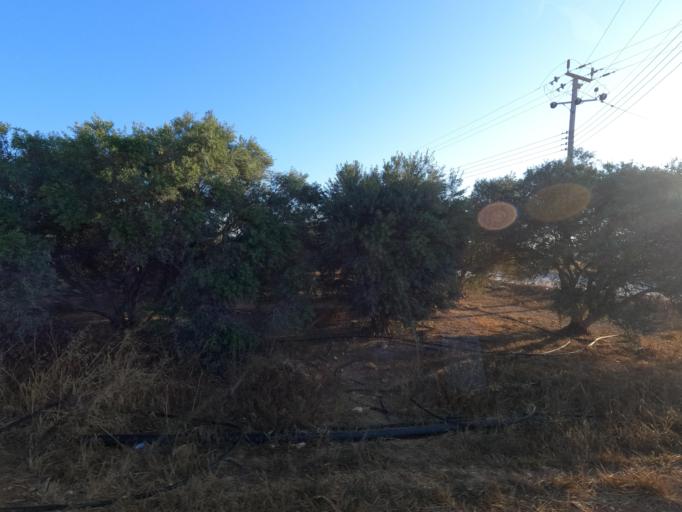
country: CY
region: Ammochostos
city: Avgorou
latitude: 35.0095
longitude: 33.8042
